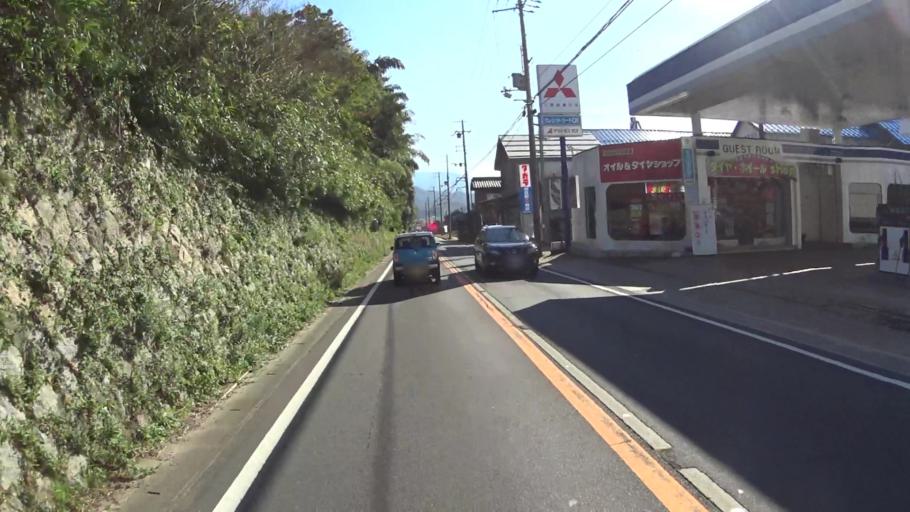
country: JP
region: Kyoto
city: Miyazu
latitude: 35.6175
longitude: 135.0612
